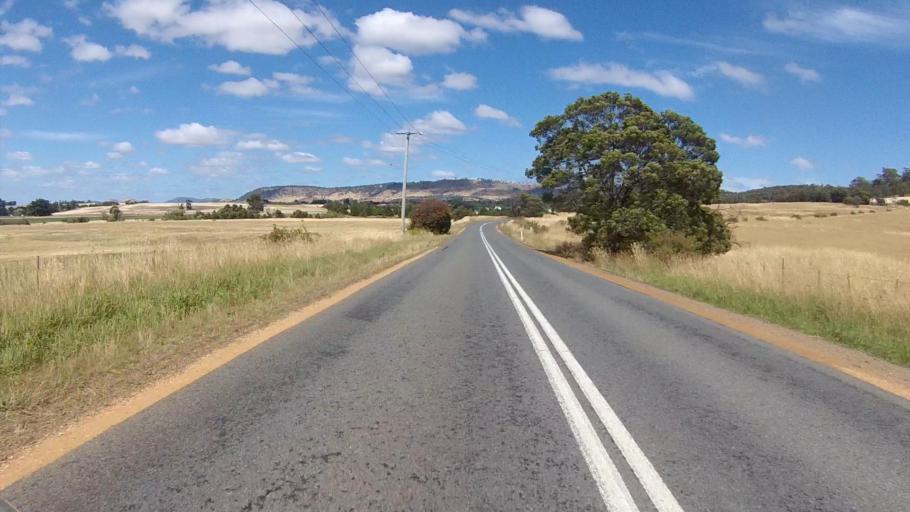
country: AU
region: Tasmania
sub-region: Clarence
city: Cambridge
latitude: -42.6550
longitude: 147.4324
